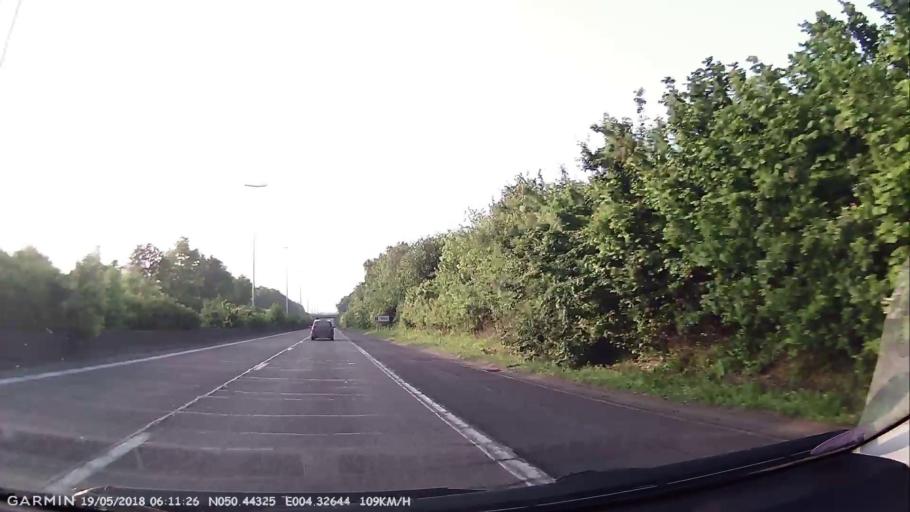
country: BE
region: Wallonia
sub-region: Province du Hainaut
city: Courcelles
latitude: 50.4432
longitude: 4.3265
